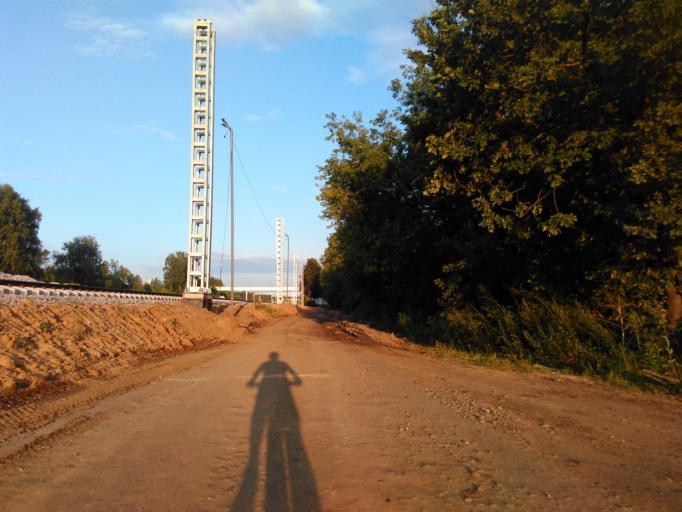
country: RU
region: Moscow
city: Rostokino
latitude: 55.8328
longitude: 37.6916
